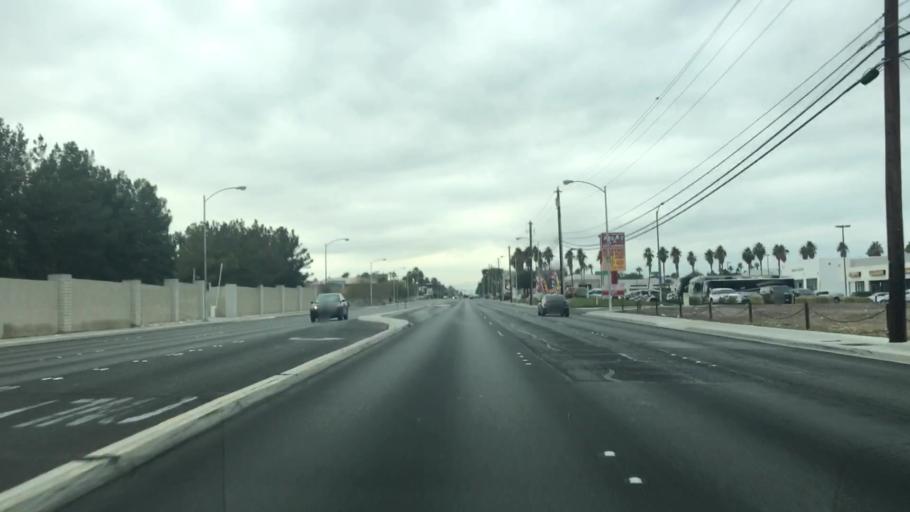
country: US
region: Nevada
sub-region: Clark County
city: Whitney
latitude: 36.0716
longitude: -115.1038
